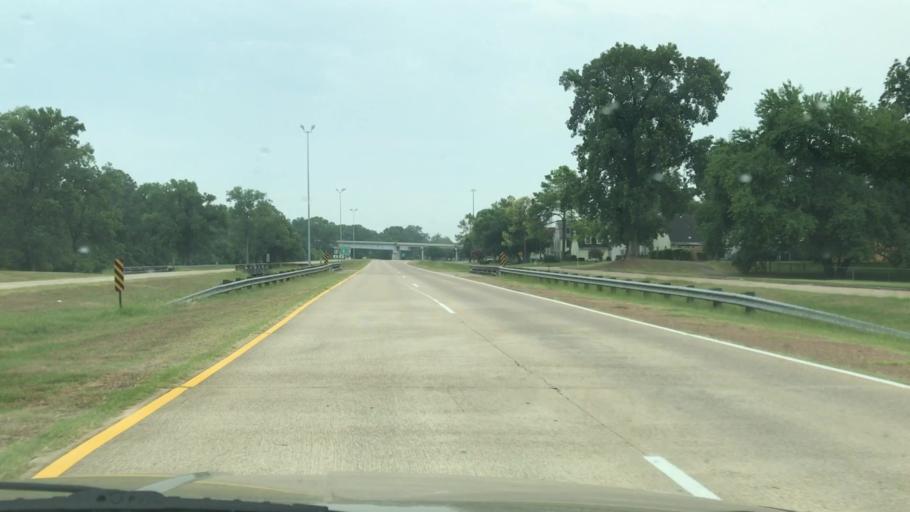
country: US
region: Louisiana
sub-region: Bossier Parish
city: Bossier City
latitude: 32.4939
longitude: -93.7060
